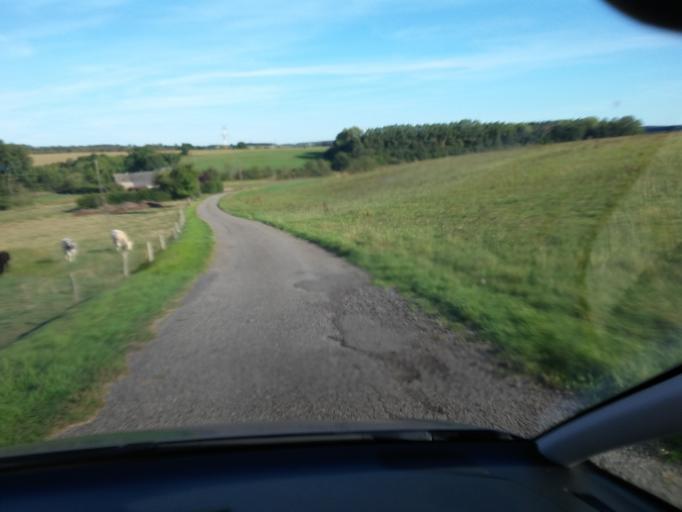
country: BE
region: Wallonia
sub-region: Province du Luxembourg
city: Habay-la-Vieille
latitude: 49.7078
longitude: 5.7021
